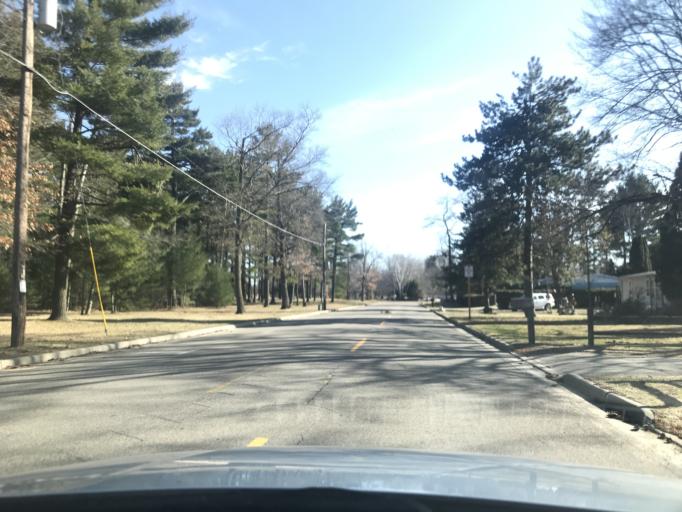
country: US
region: Wisconsin
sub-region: Marinette County
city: Marinette
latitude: 45.0902
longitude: -87.6398
